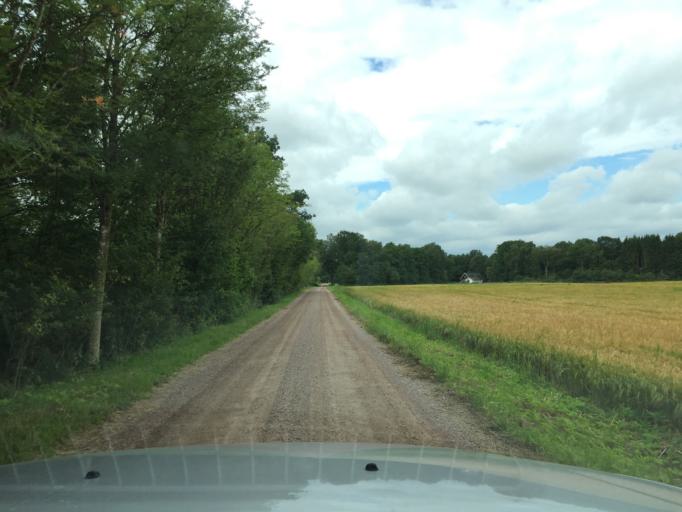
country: SE
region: Skane
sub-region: Hassleholms Kommun
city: Sosdala
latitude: 56.0249
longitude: 13.7027
